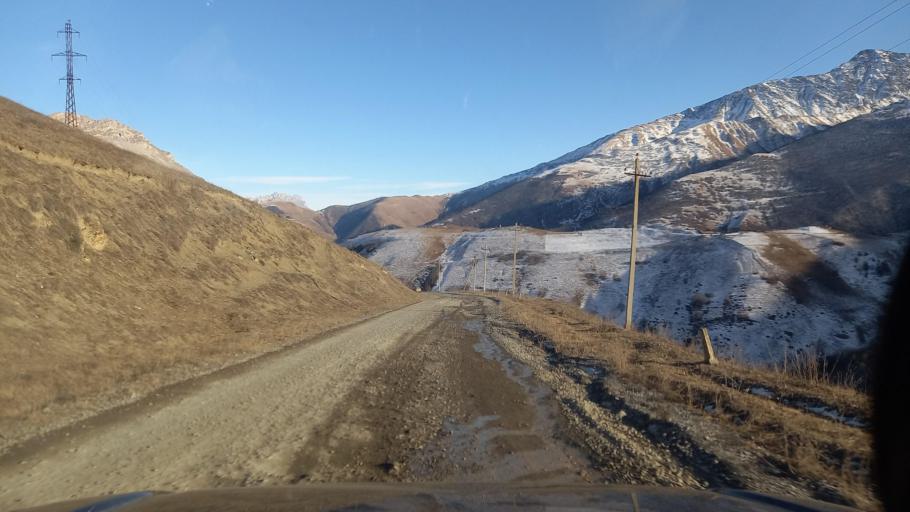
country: RU
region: North Ossetia
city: Verkhniy Fiagdon
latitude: 42.8344
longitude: 44.4833
